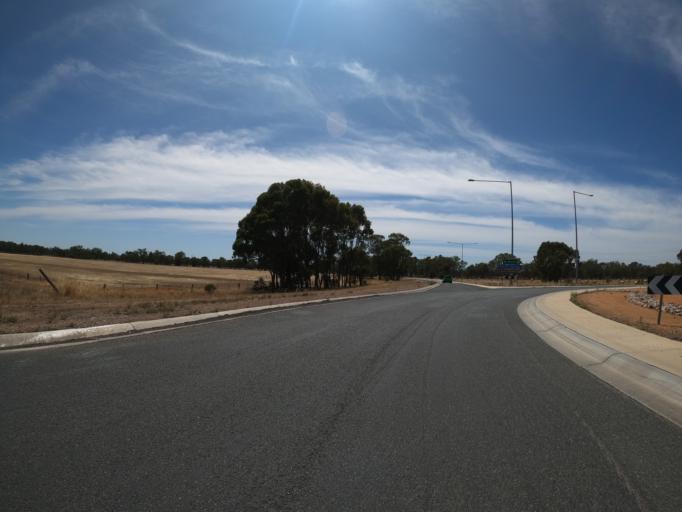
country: AU
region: Victoria
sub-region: Benalla
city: Benalla
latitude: -36.5197
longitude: 146.0648
